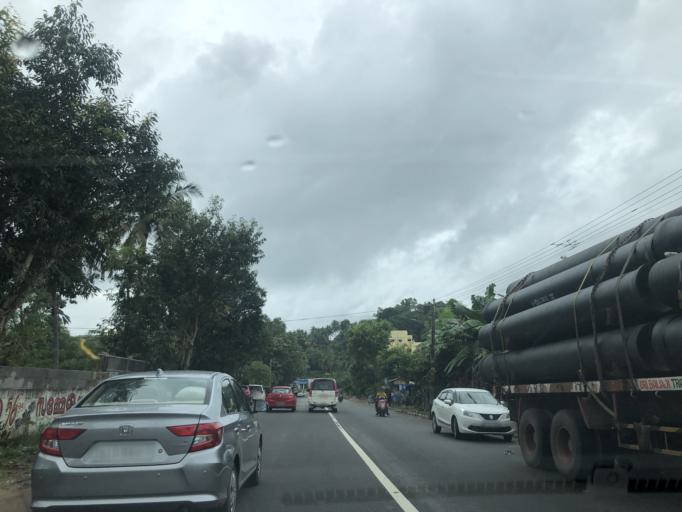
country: IN
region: Kerala
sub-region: Thiruvananthapuram
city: Thiruvananthapuram
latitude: 8.5139
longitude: 76.9145
